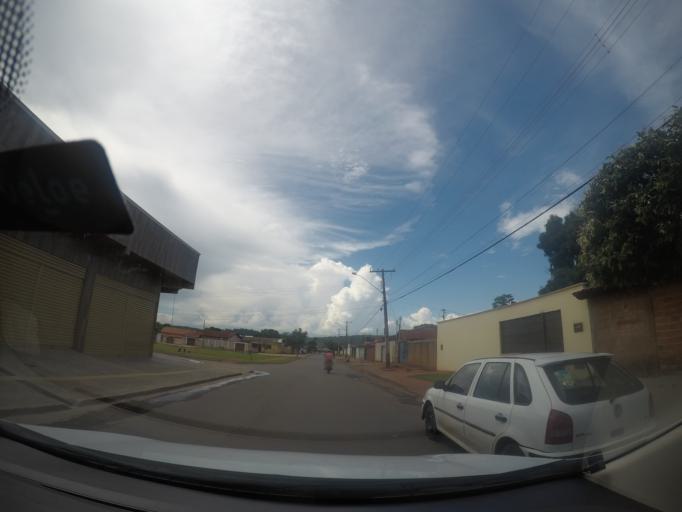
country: BR
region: Goias
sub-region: Goiania
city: Goiania
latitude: -16.6986
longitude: -49.3563
